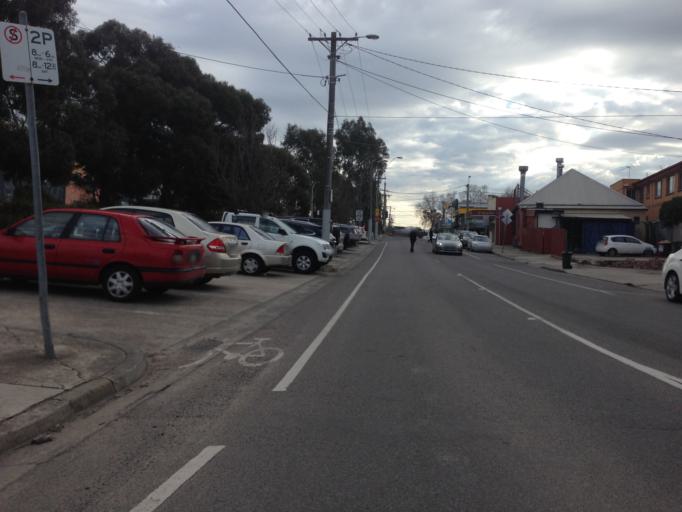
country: AU
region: Victoria
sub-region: Darebin
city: Fairfield
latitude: -37.7789
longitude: 145.0191
